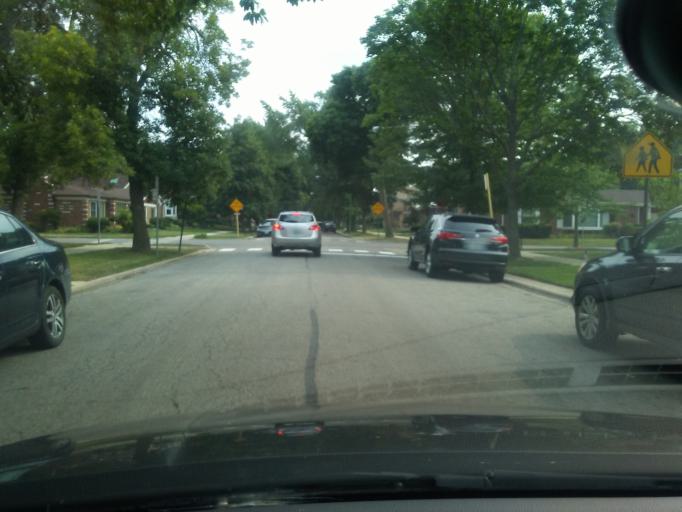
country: US
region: Illinois
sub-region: Cook County
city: Lincolnwood
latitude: 41.9941
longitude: -87.7252
